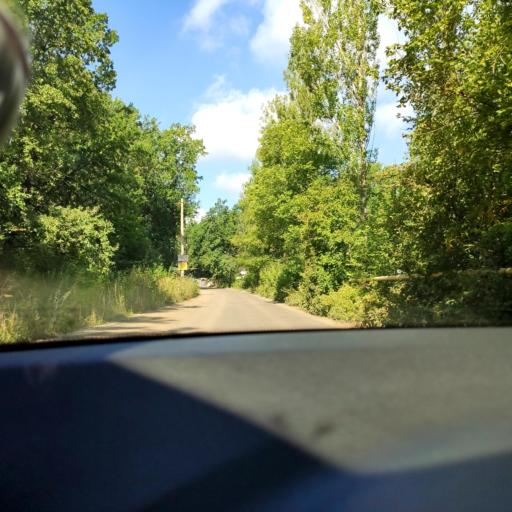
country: RU
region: Samara
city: Volzhskiy
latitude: 53.4325
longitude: 50.0828
